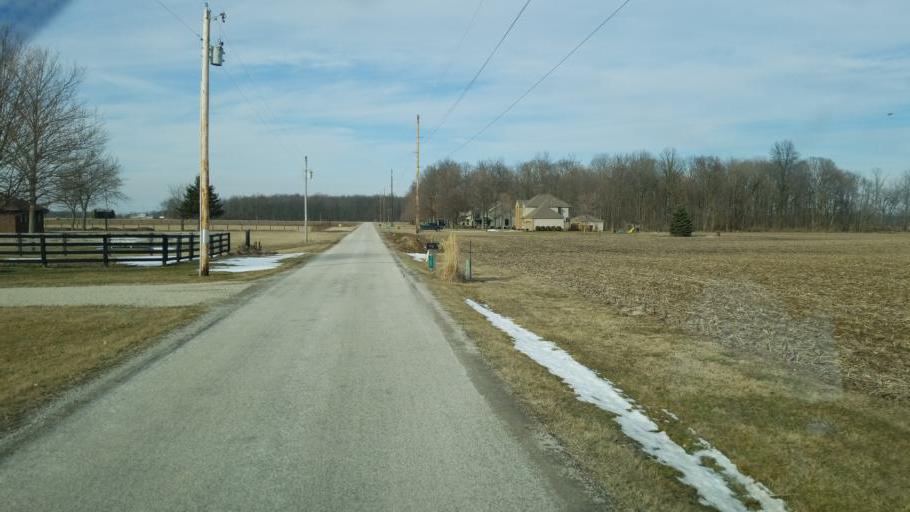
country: US
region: Ohio
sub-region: Marion County
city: Prospect
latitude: 40.4453
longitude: -83.2061
